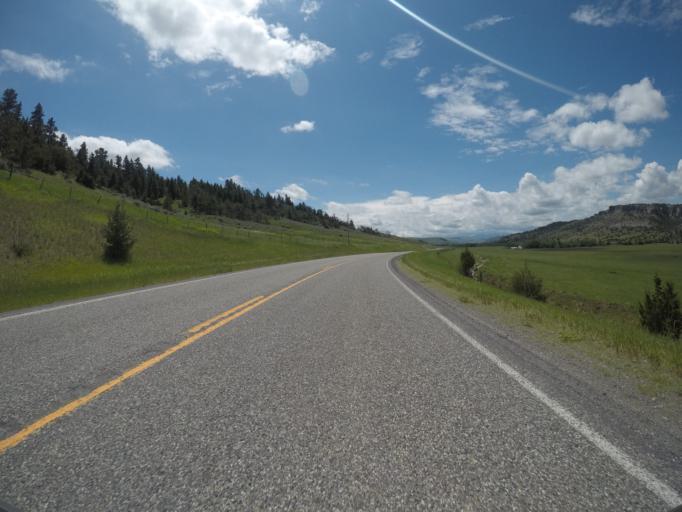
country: US
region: Montana
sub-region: Sweet Grass County
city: Big Timber
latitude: 45.7145
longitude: -110.0000
